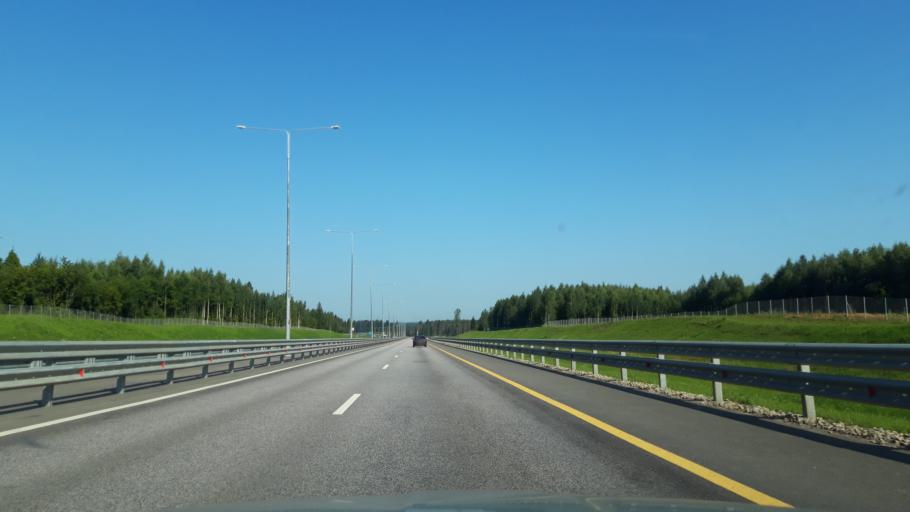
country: RU
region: Moskovskaya
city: Klin
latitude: 56.2877
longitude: 36.7056
